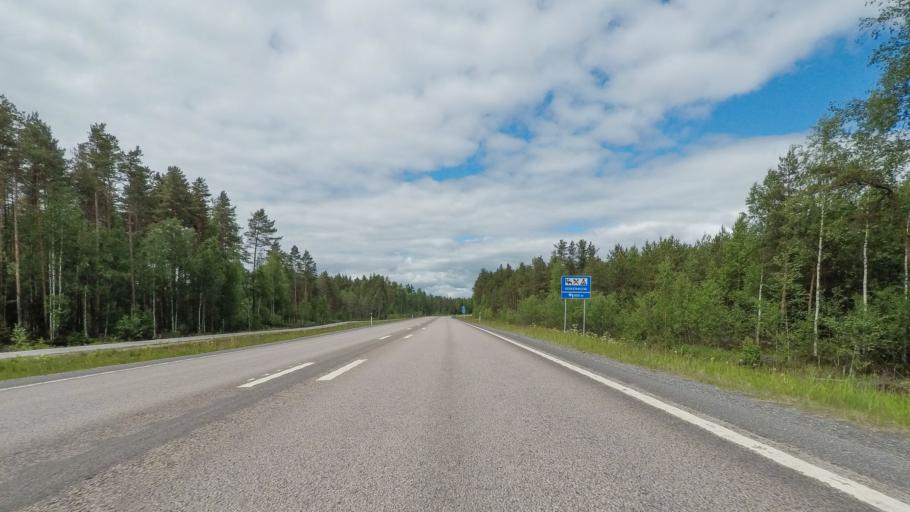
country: FI
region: Paijanne Tavastia
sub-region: Lahti
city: Hartola
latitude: 61.5548
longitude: 26.0079
